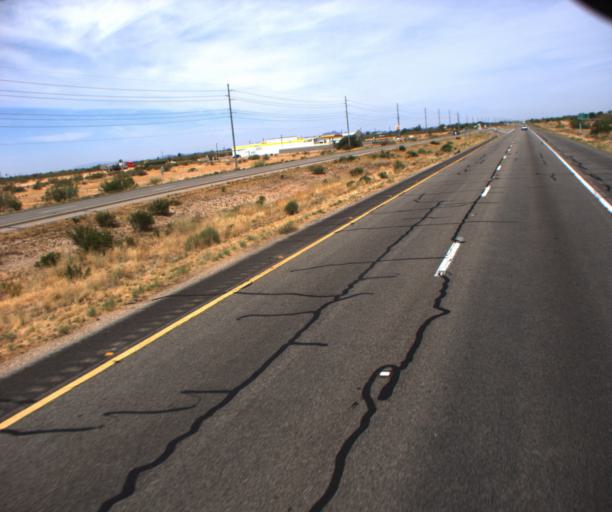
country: US
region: Arizona
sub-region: Maricopa County
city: Sun City West
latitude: 33.7644
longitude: -112.5111
